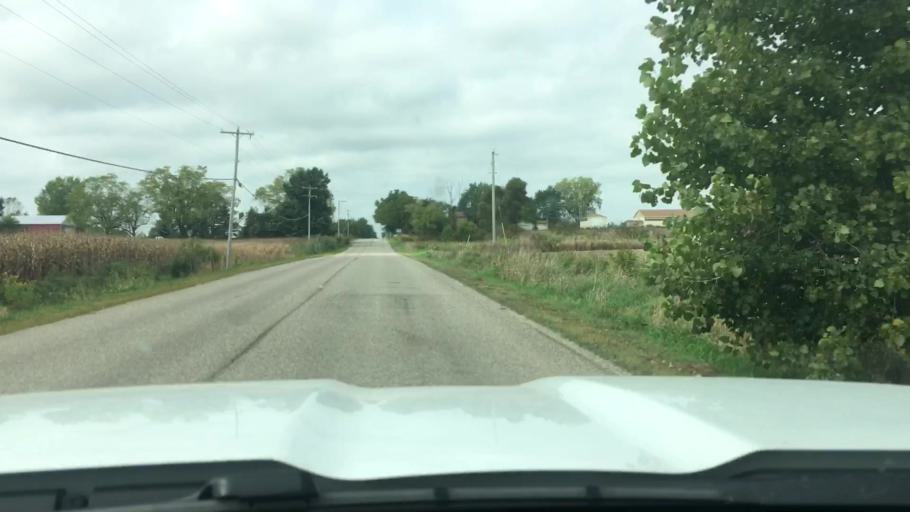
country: US
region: Michigan
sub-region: Eaton County
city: Potterville
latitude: 42.6256
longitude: -84.7084
